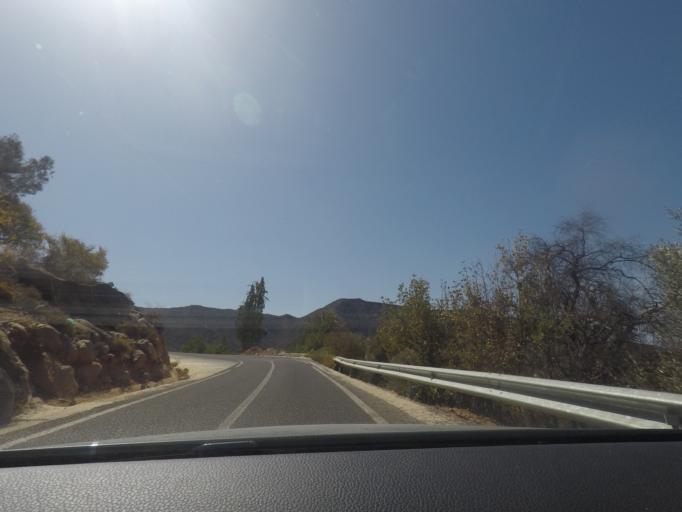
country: MA
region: Souss-Massa-Draa
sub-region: Agadir-Ida-ou-Tnan
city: Aourir
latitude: 30.5986
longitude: -9.5122
